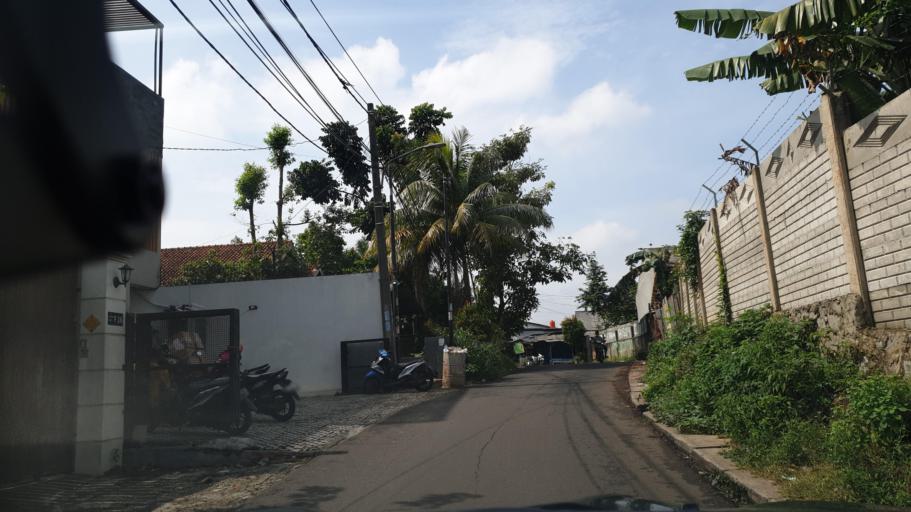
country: ID
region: West Java
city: Pamulang
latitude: -6.3207
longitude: 106.7553
